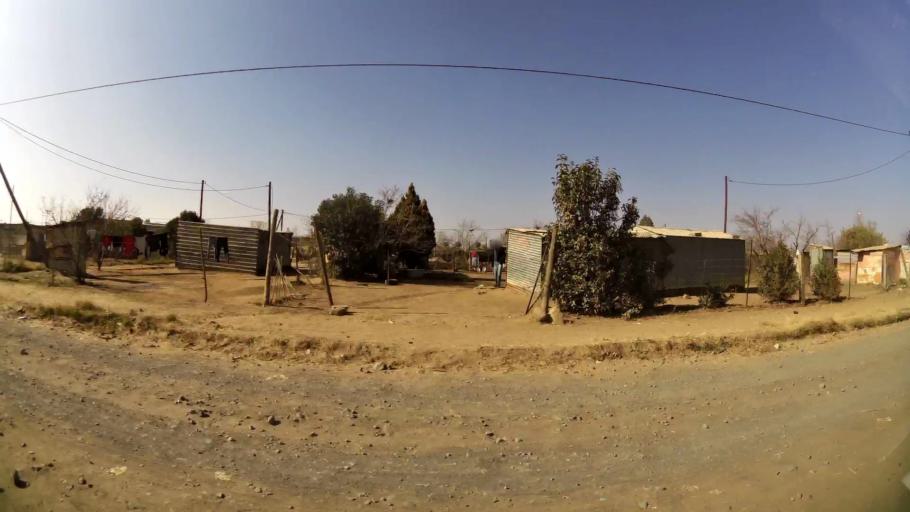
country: ZA
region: Orange Free State
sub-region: Mangaung Metropolitan Municipality
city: Bloemfontein
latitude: -29.1747
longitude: 26.2906
